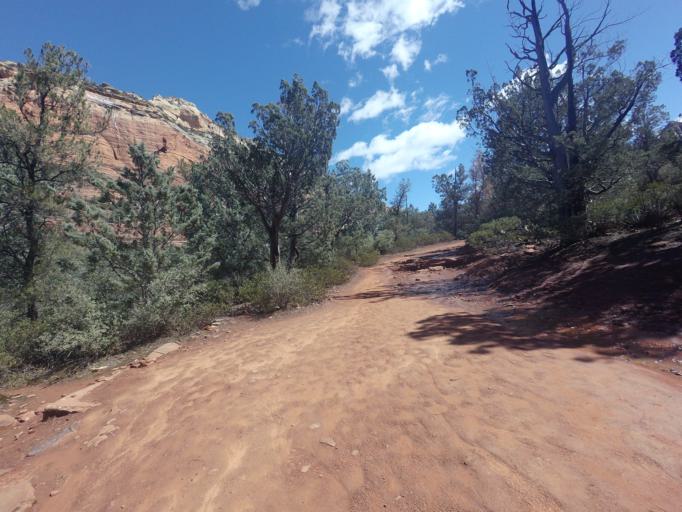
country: US
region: Arizona
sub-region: Yavapai County
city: West Sedona
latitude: 34.9020
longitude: -111.8095
